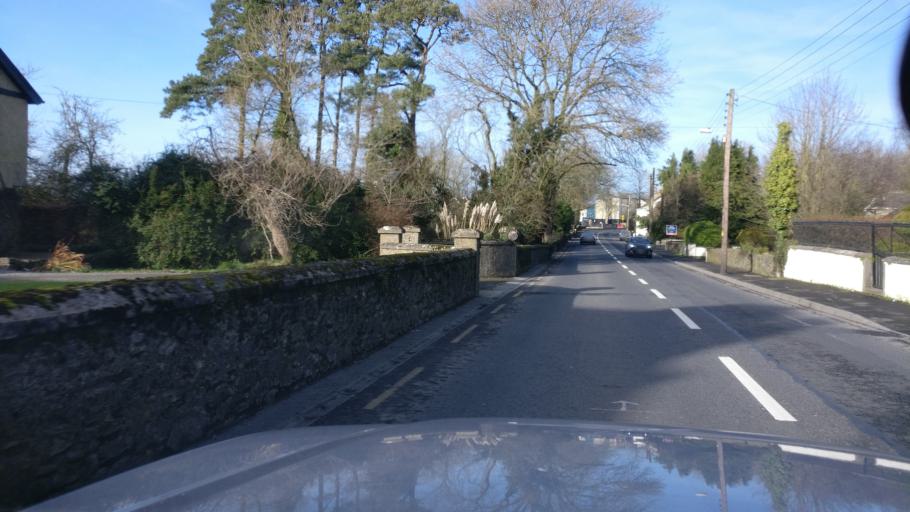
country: IE
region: Leinster
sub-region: Laois
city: Mountmellick
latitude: 53.1128
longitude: -7.3287
